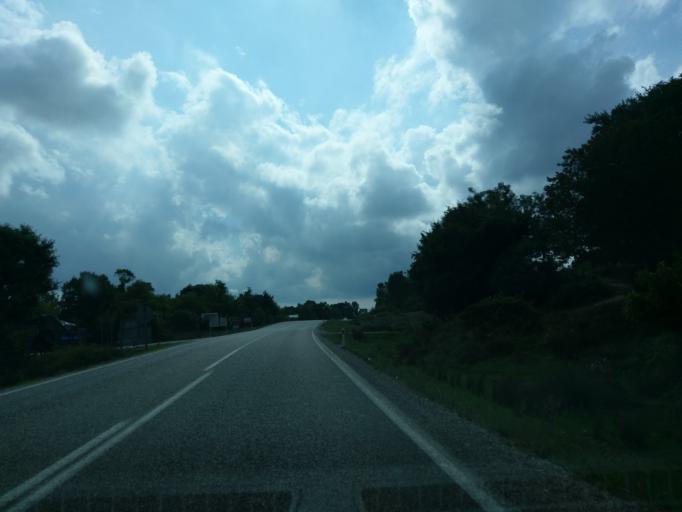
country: TR
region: Sinop
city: Sinop
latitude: 42.0225
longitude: 35.0463
